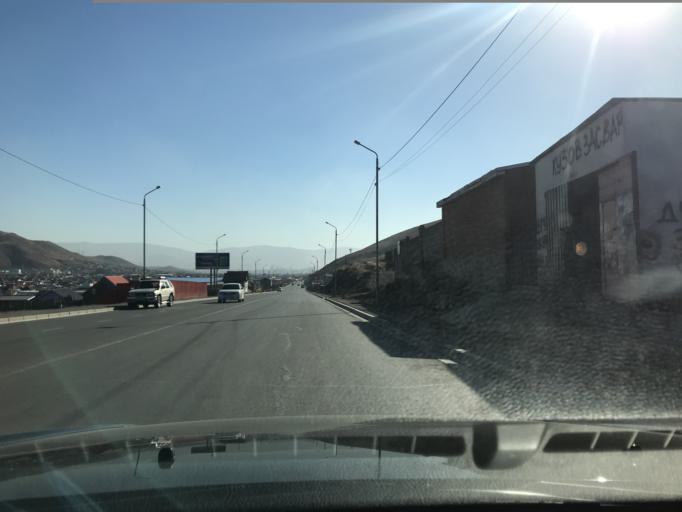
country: MN
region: Ulaanbaatar
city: Ulaanbaatar
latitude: 47.9929
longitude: 106.9257
